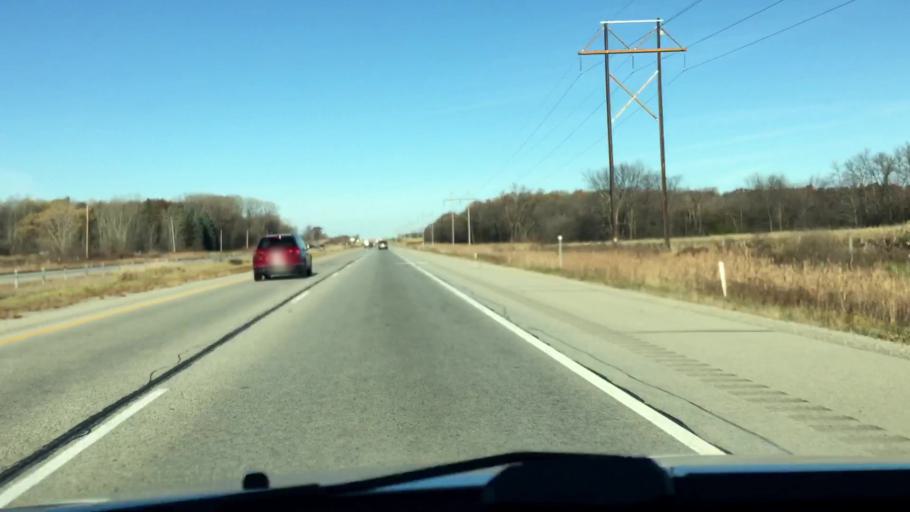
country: US
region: Wisconsin
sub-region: Fond du Lac County
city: North Fond du Lac
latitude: 43.8359
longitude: -88.5472
